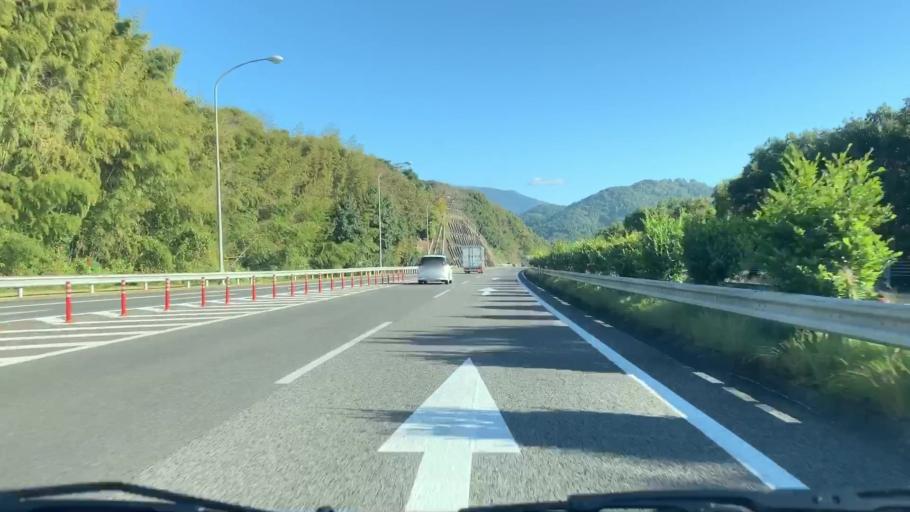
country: JP
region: Saga Prefecture
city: Takeocho-takeo
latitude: 33.2629
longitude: 130.0839
